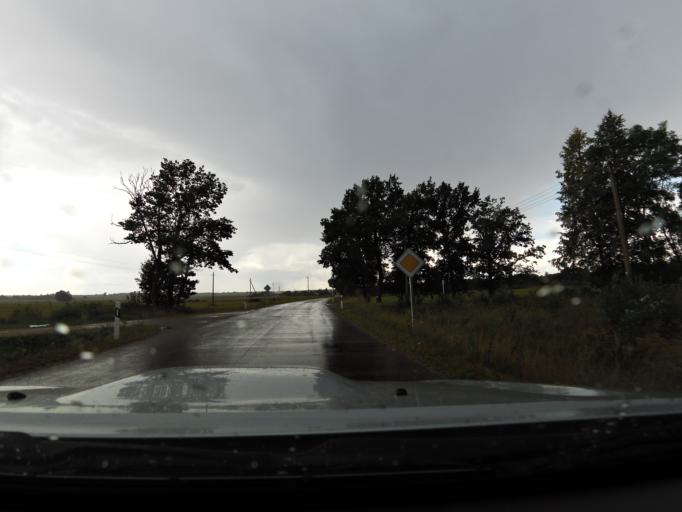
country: LT
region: Vilnius County
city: Ukmerge
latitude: 55.2837
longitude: 24.5130
